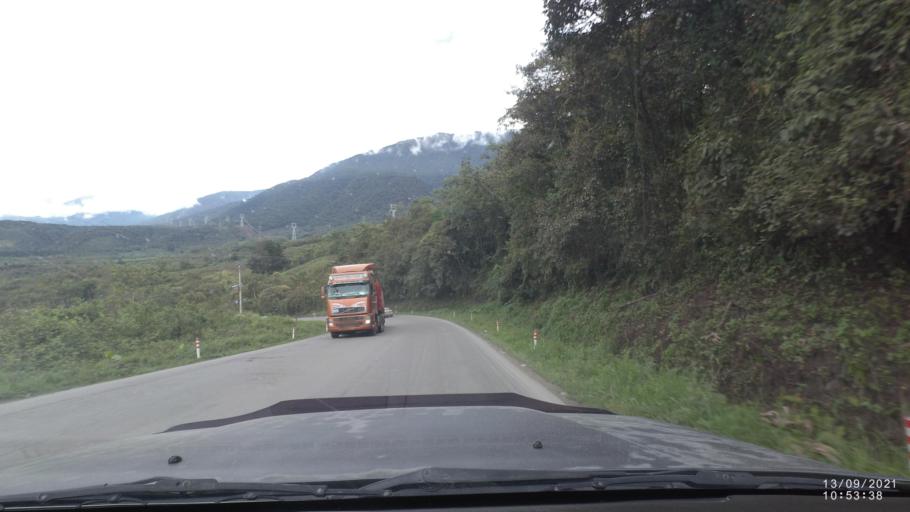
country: BO
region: Cochabamba
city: Colomi
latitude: -17.2053
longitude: -65.8292
